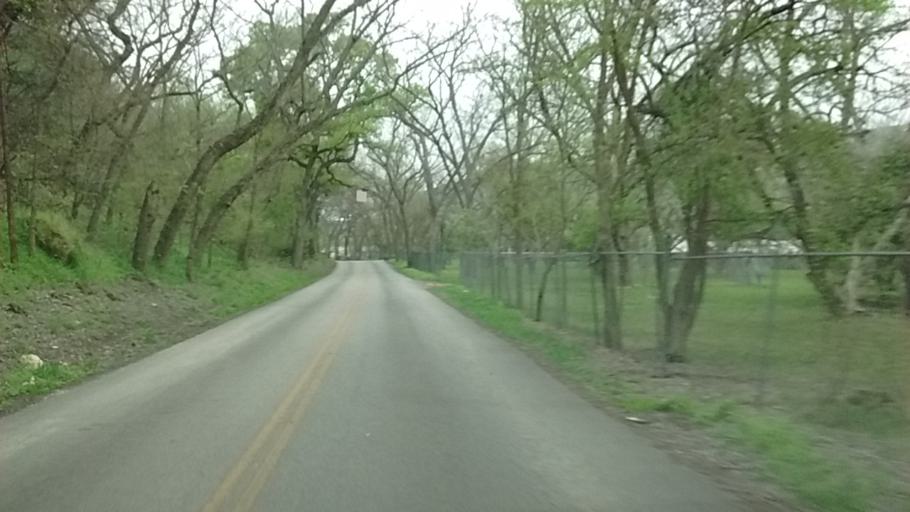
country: US
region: Texas
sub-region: Comal County
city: New Braunfels
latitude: 29.8035
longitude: -98.1497
